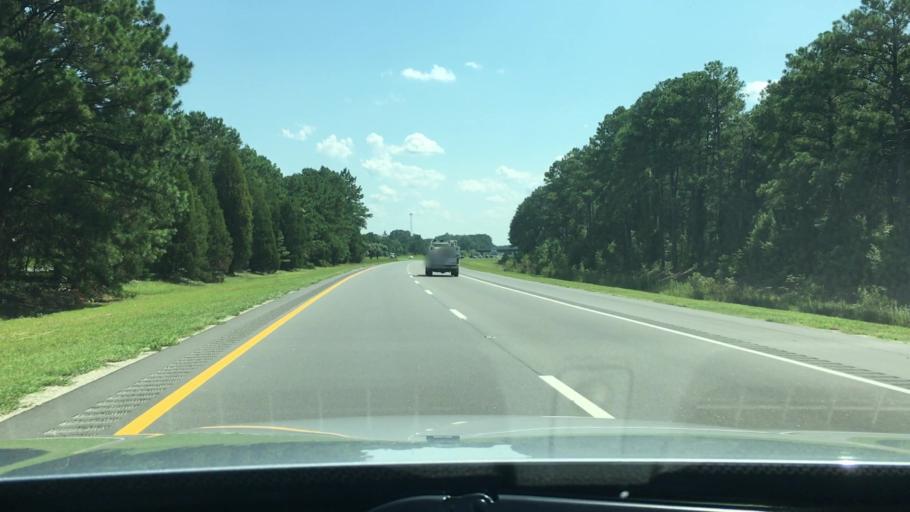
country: US
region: North Carolina
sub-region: Cumberland County
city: Vander
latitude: 35.0603
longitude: -78.7950
